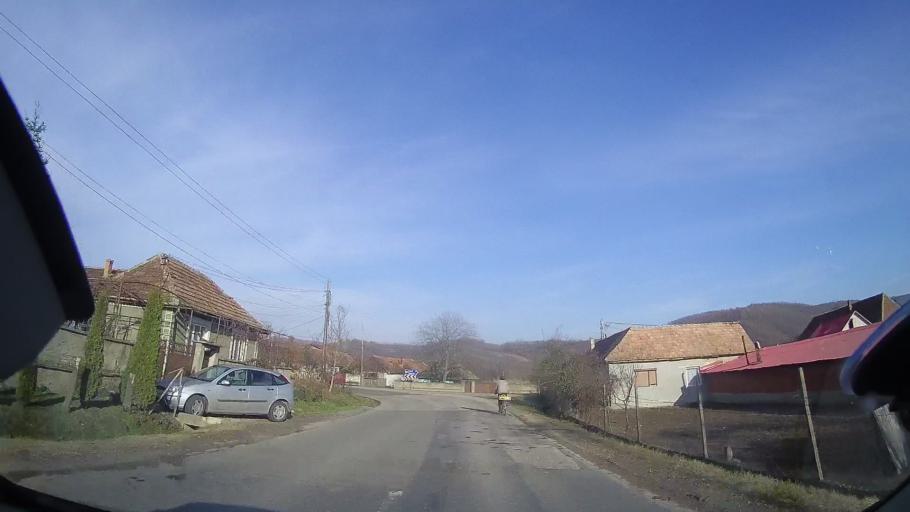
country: RO
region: Bihor
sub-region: Comuna Brusturi
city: Brusturi
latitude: 47.1366
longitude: 22.2688
